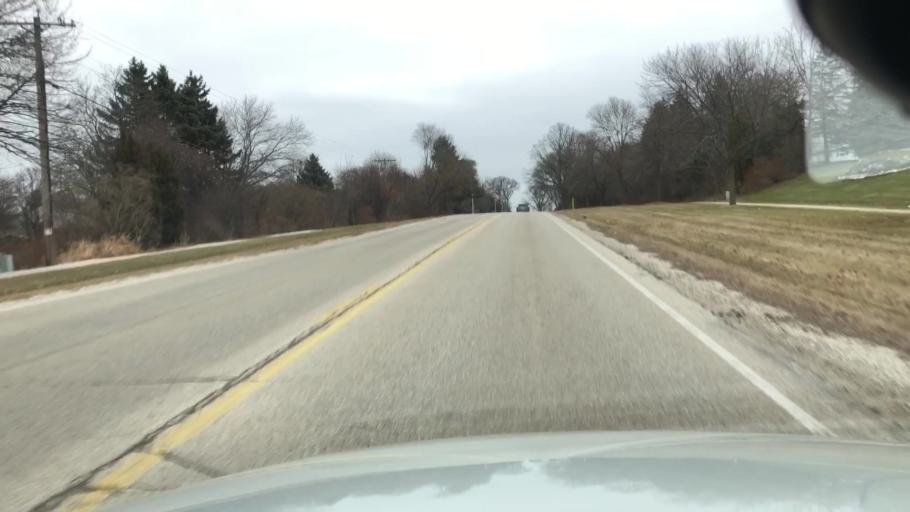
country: US
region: Wisconsin
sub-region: Waukesha County
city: Brookfield
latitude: 43.0612
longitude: -88.1387
